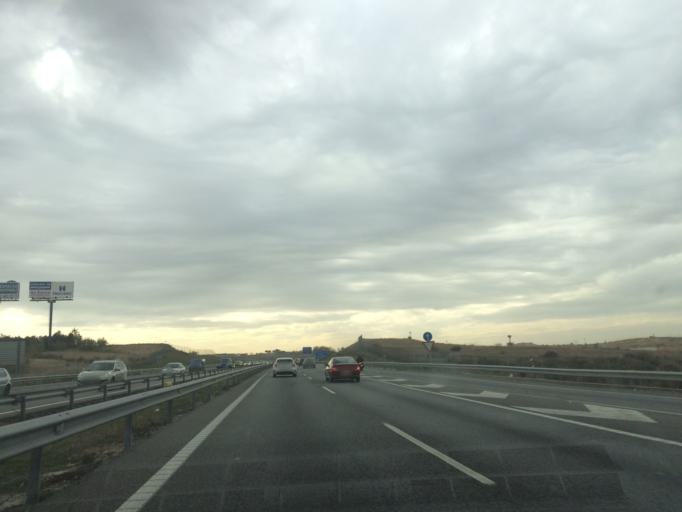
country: ES
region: Madrid
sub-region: Provincia de Madrid
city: Mostoles
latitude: 40.3154
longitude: -3.8982
